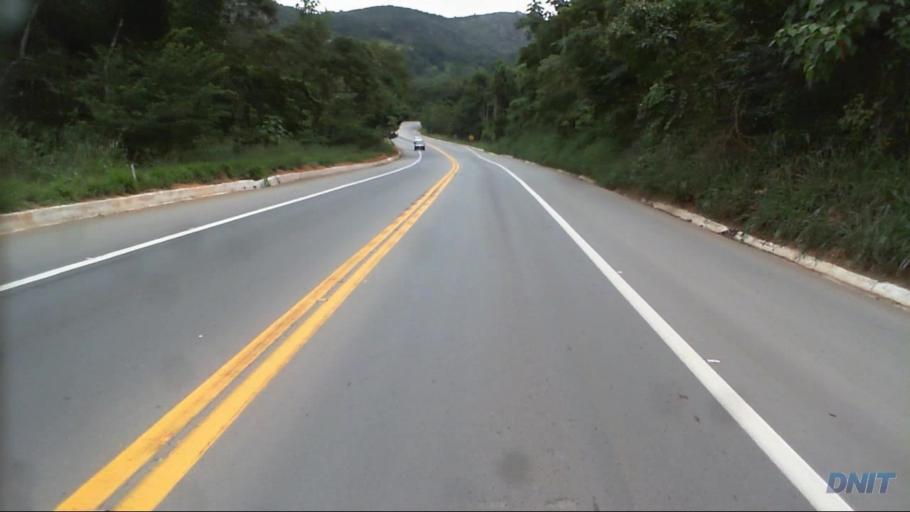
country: BR
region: Minas Gerais
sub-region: Barao De Cocais
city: Barao de Cocais
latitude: -19.7379
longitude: -43.5096
